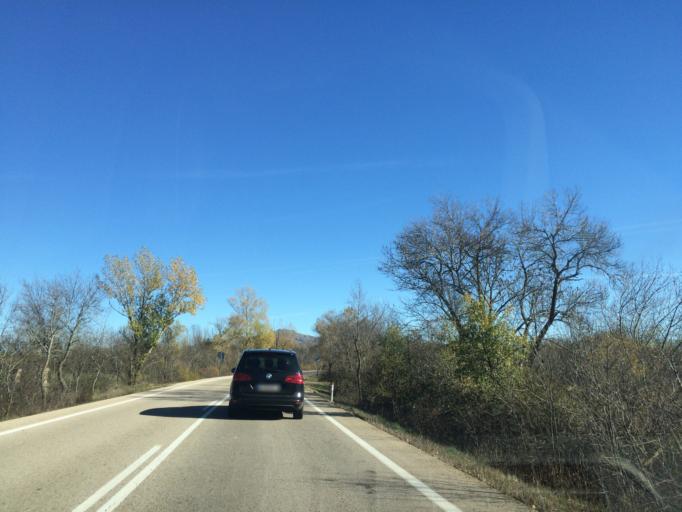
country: ES
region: Madrid
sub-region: Provincia de Madrid
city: Manzanares el Real
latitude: 40.7391
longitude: -3.8066
